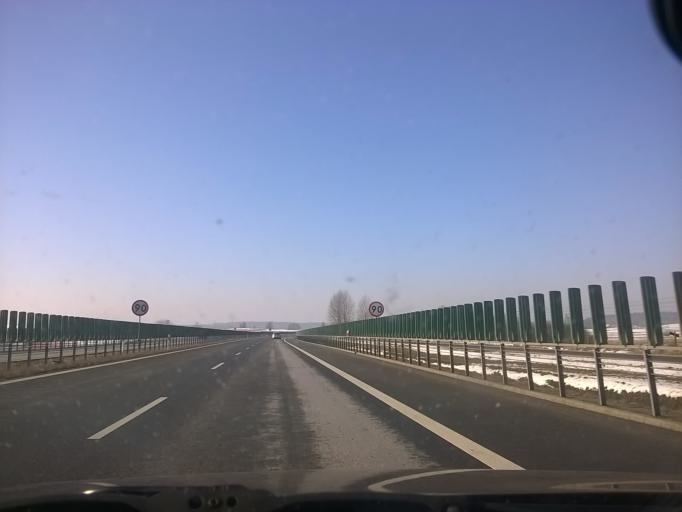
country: PL
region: Warmian-Masurian Voivodeship
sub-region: Powiat olsztynski
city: Biskupiec
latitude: 53.8353
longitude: 21.0299
